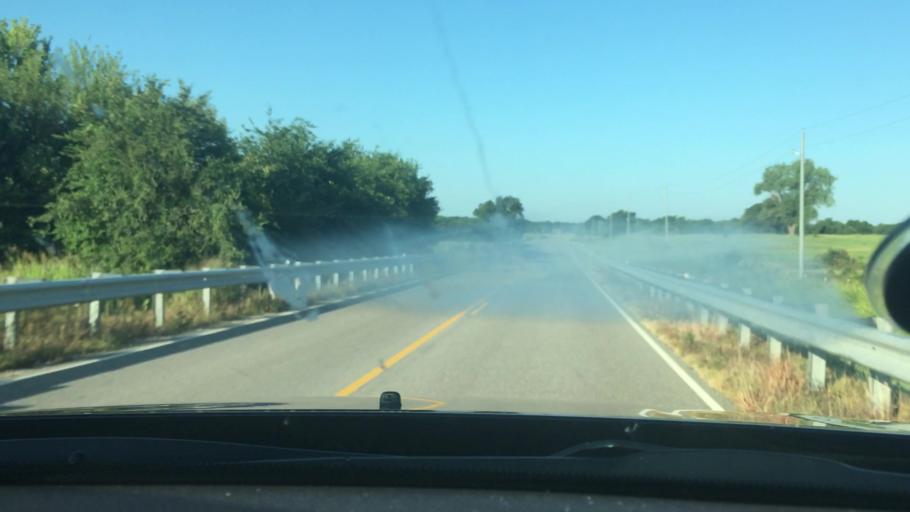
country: US
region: Oklahoma
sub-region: Pontotoc County
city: Ada
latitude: 34.6430
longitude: -96.8061
